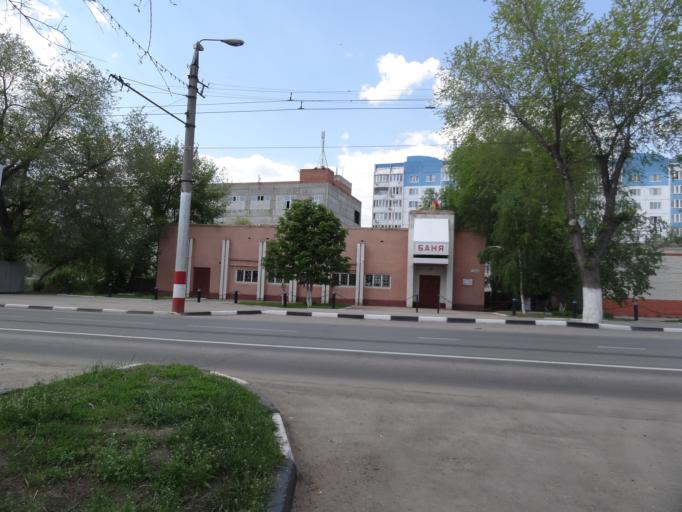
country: RU
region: Saratov
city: Engel's
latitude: 51.5028
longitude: 46.1116
